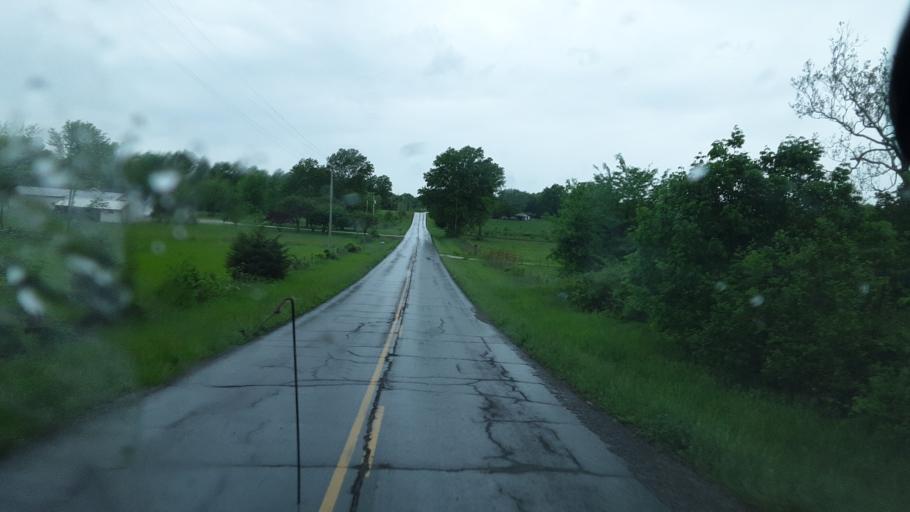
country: US
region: Missouri
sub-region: Boone County
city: Centralia
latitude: 39.3885
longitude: -92.2248
